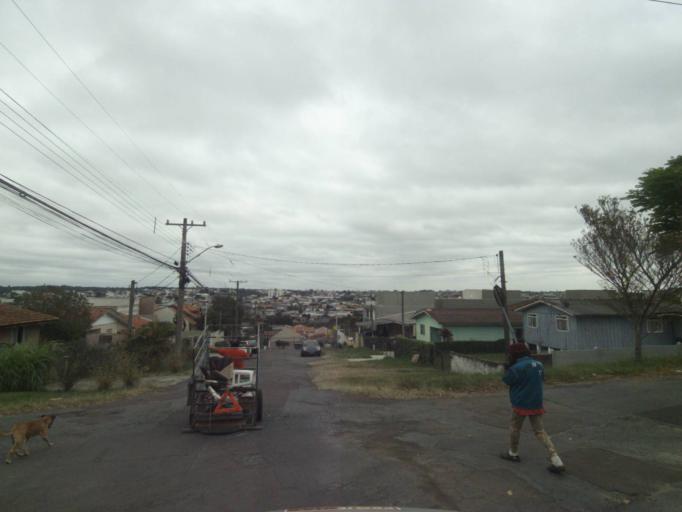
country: BR
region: Parana
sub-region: Sao Jose Dos Pinhais
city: Sao Jose dos Pinhais
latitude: -25.4857
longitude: -49.2299
